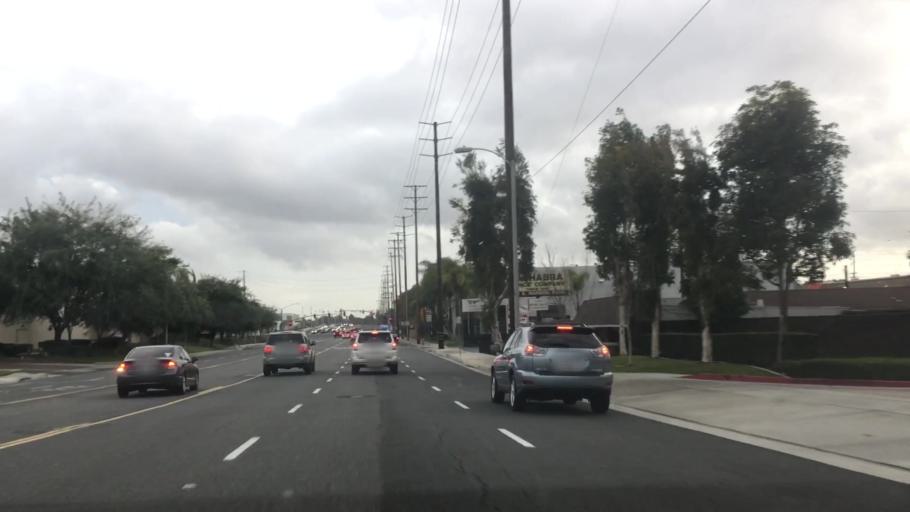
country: US
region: California
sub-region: Orange County
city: La Habra
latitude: 33.9273
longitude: -117.9332
